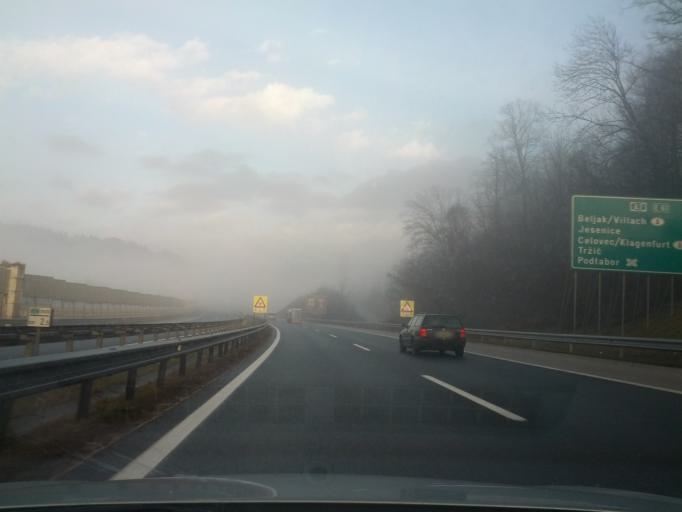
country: SI
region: Naklo
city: Naklo
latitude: 46.2884
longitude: 14.2880
